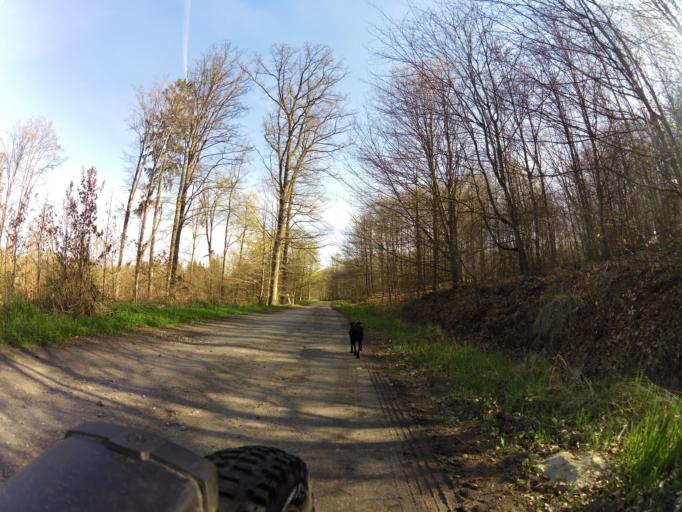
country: PL
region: West Pomeranian Voivodeship
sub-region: Powiat lobeski
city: Lobez
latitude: 53.7648
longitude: 15.5873
